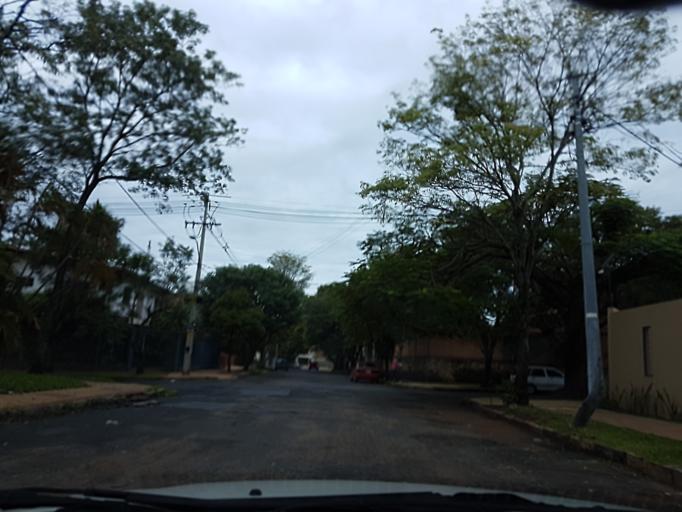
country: PY
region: Asuncion
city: Asuncion
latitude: -25.2858
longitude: -57.6005
